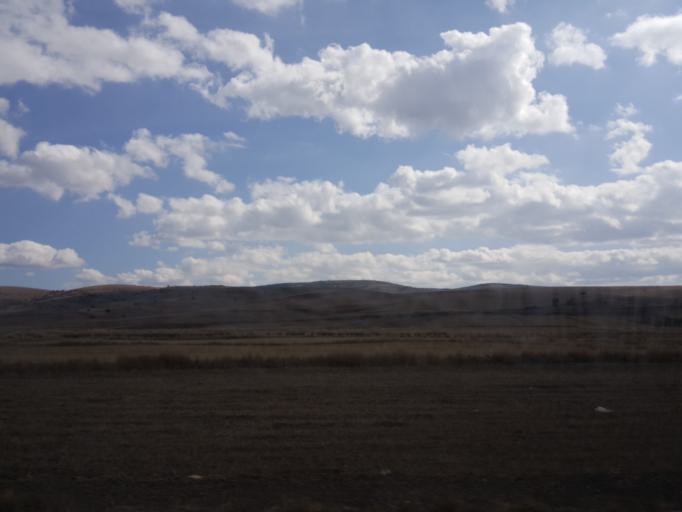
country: TR
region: Tokat
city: Artova
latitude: 40.1240
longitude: 36.3246
